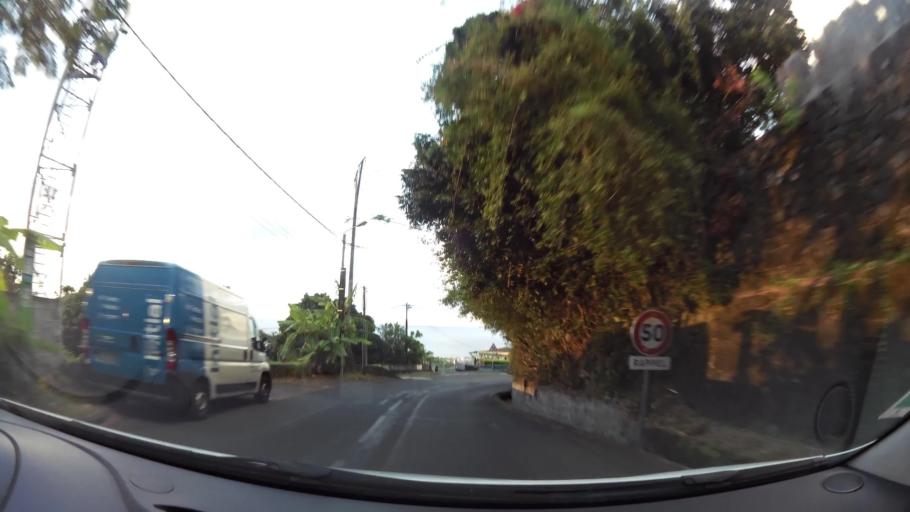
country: RE
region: Reunion
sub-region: Reunion
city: Saint-Denis
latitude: -20.9085
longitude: 55.4629
